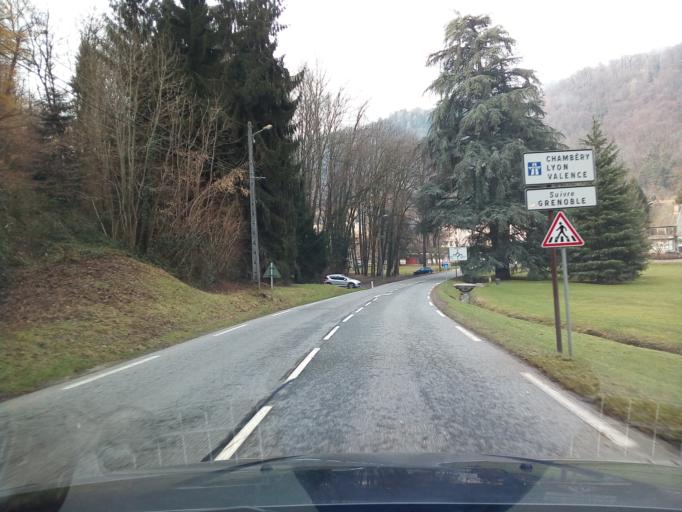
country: FR
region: Rhone-Alpes
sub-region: Departement de l'Isere
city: Vaulnaveys-le-Haut
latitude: 45.1394
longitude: 5.8298
